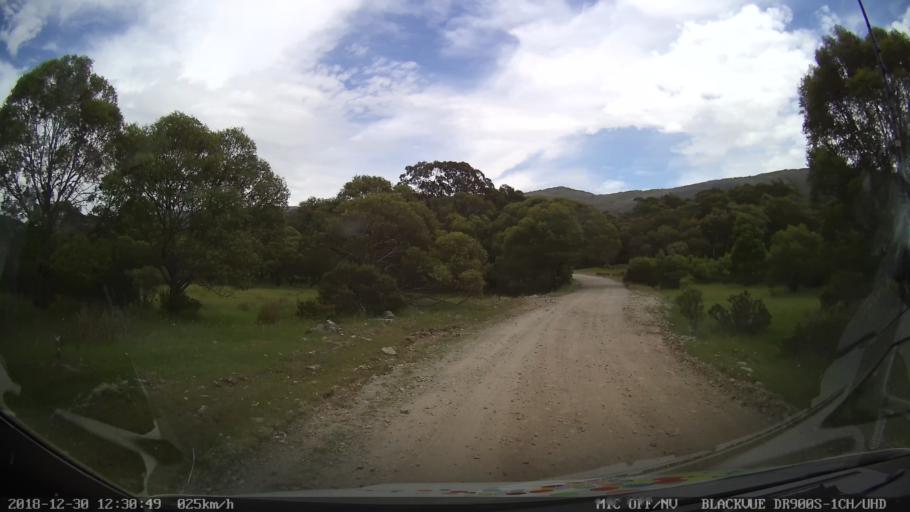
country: AU
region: New South Wales
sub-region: Snowy River
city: Jindabyne
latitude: -36.3244
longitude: 148.4729
